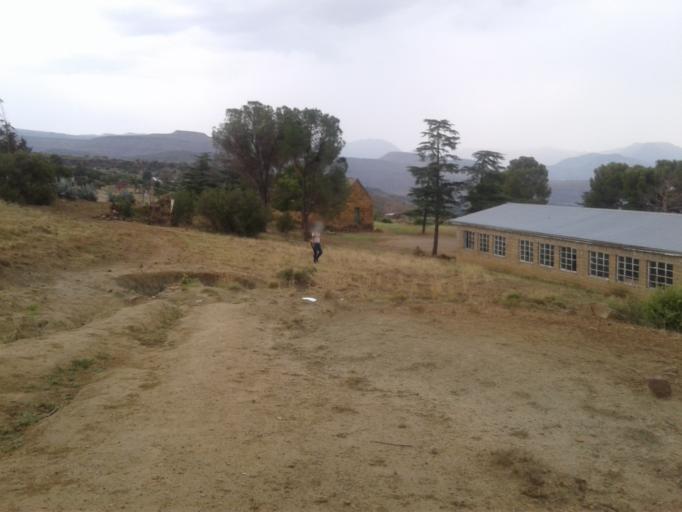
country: LS
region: Quthing
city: Quthing
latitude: -30.3857
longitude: 27.5599
